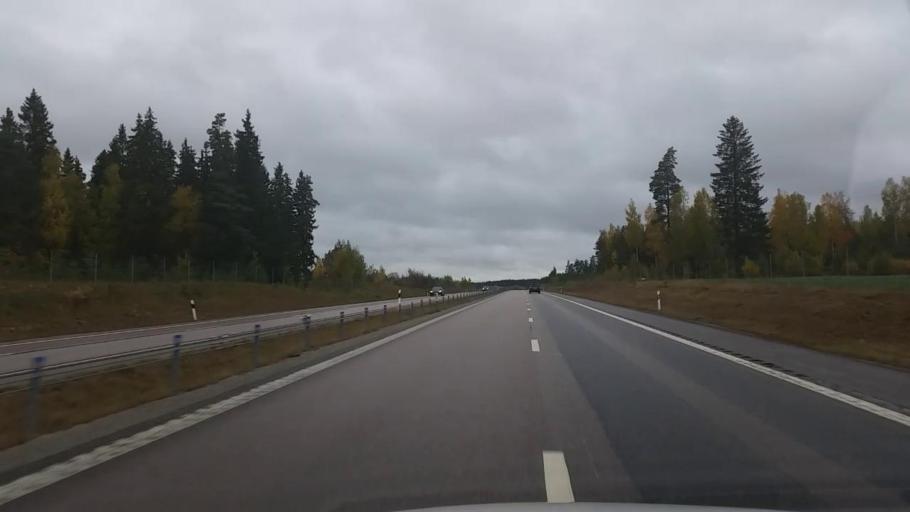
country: SE
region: Uppsala
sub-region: Osthammars Kommun
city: Bjorklinge
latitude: 60.1080
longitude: 17.5584
